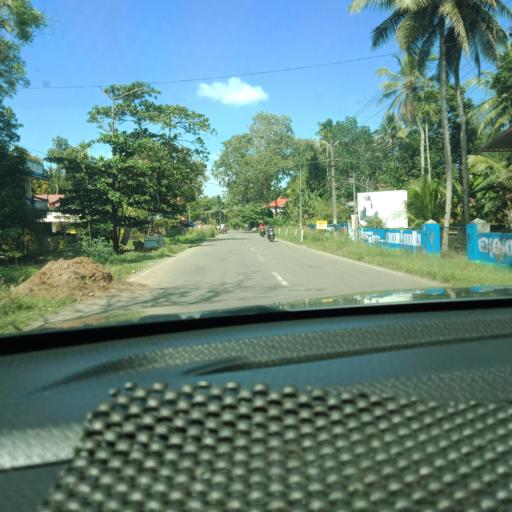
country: IN
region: Kerala
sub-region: Alappuzha
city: Mavelikara
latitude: 9.2907
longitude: 76.4561
